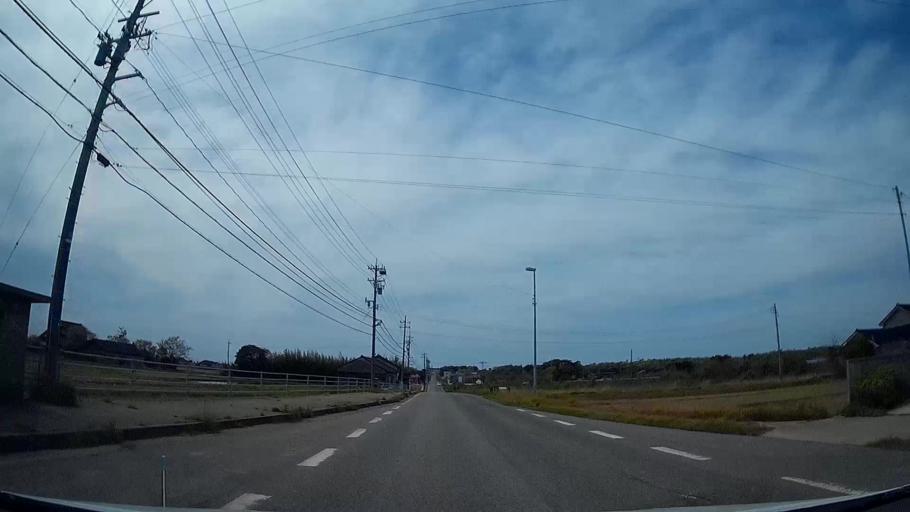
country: JP
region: Ishikawa
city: Hakui
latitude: 37.0117
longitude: 136.7602
